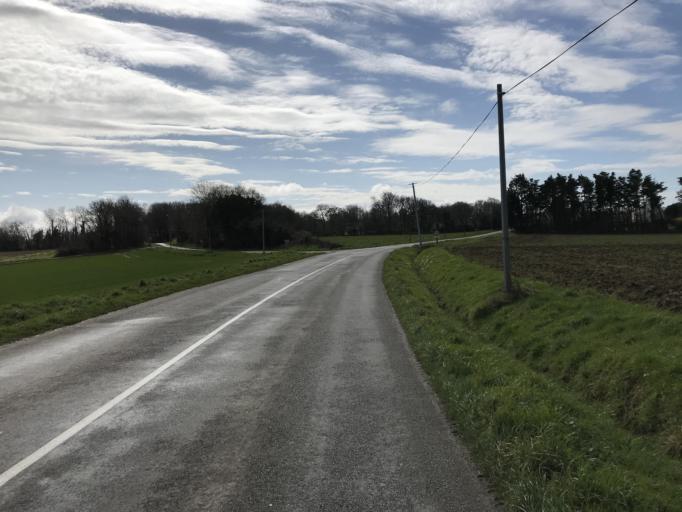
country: FR
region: Brittany
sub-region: Departement du Finistere
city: Dirinon
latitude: 48.3859
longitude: -4.2662
